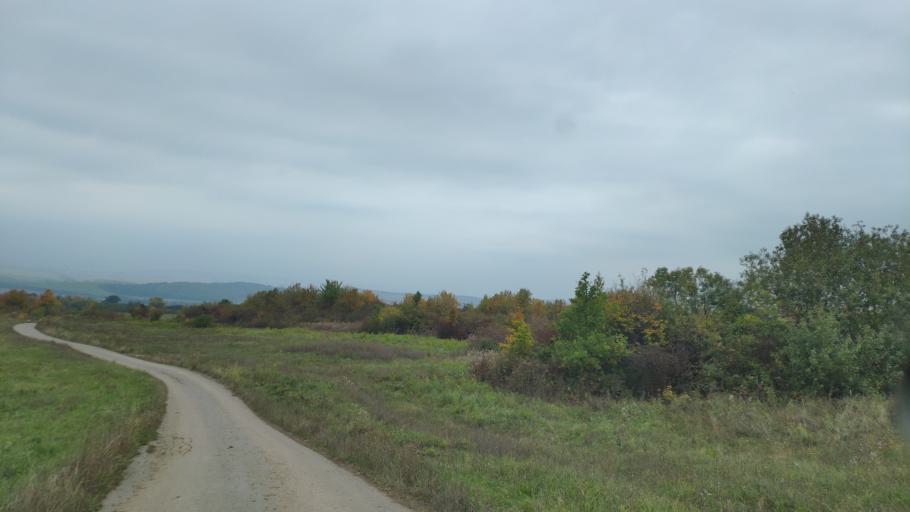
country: SK
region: Kosicky
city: Kosice
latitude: 48.6281
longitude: 21.4074
